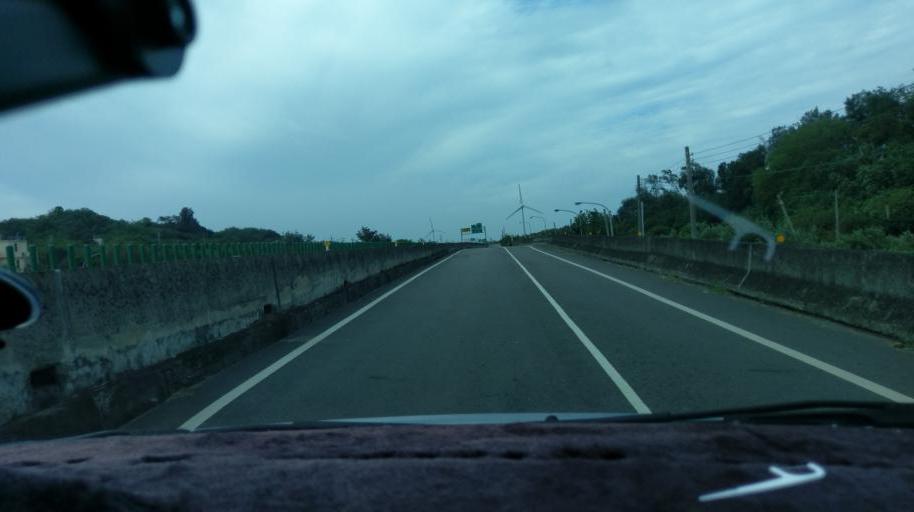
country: TW
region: Taiwan
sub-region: Hsinchu
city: Hsinchu
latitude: 24.7311
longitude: 120.8776
